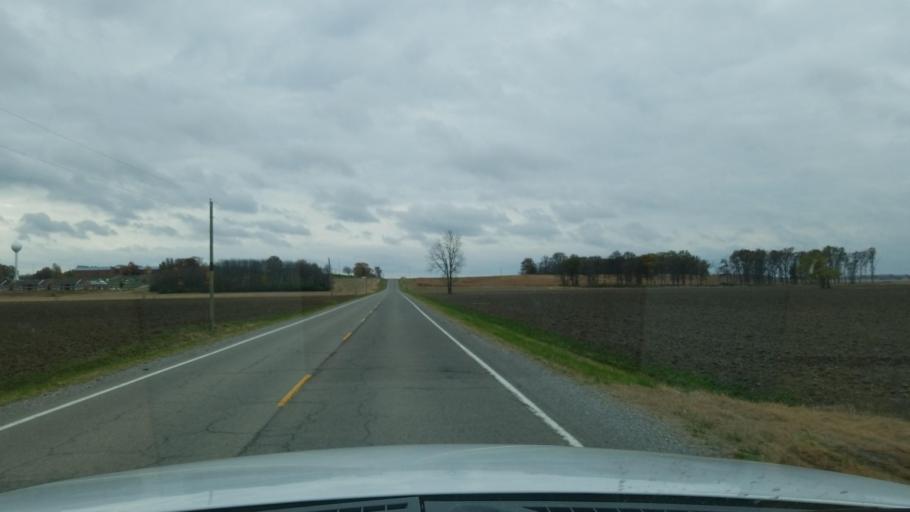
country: US
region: Illinois
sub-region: Saline County
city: Eldorado
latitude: 37.7598
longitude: -88.4383
